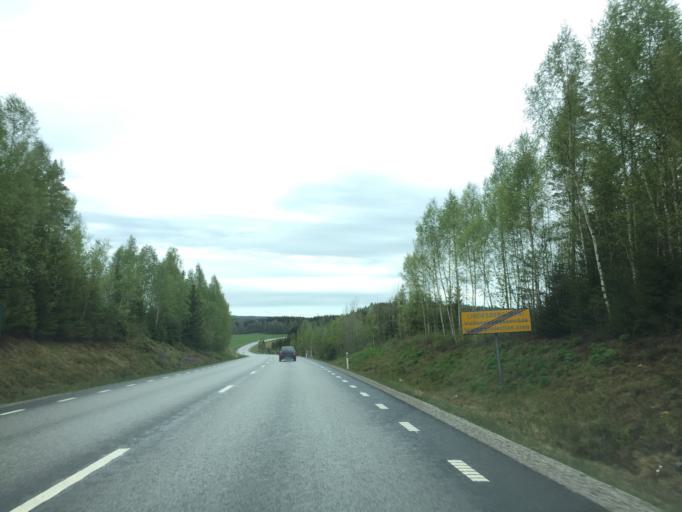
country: SE
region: OErebro
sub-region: Lindesbergs Kommun
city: Lindesberg
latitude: 59.5662
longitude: 15.2153
